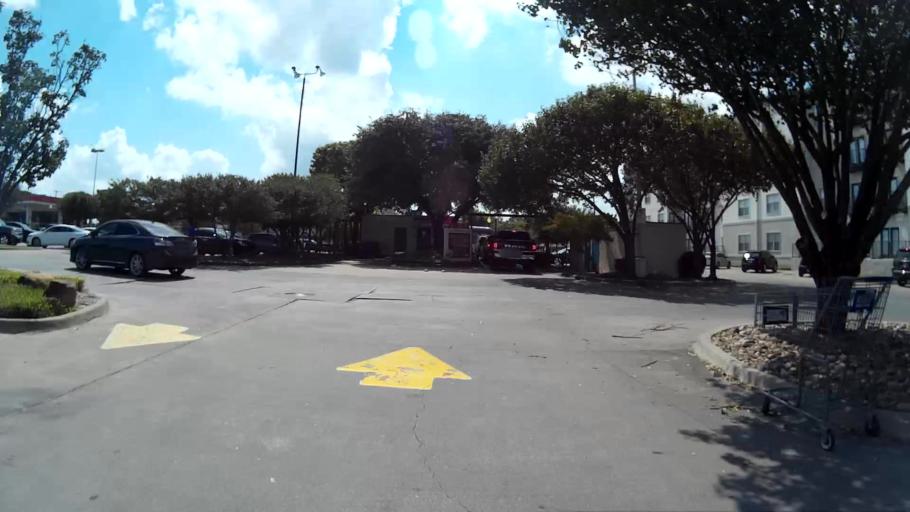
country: US
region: Texas
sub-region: Dallas County
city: Highland Park
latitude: 32.8400
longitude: -96.7716
